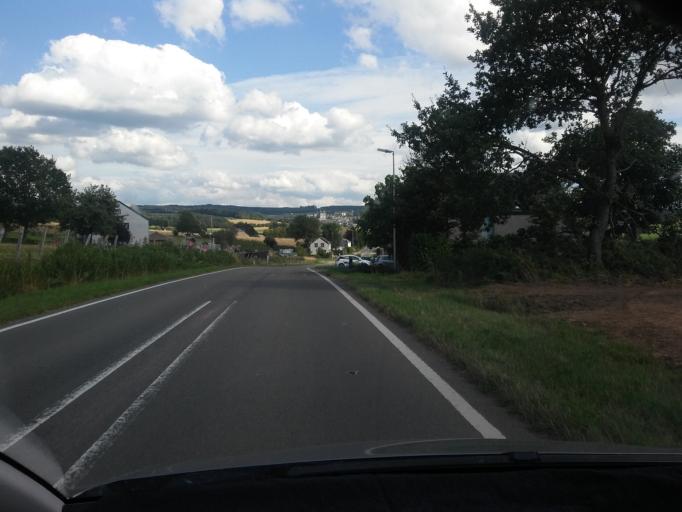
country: BE
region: Wallonia
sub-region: Province du Luxembourg
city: Saint-Hubert
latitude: 50.0300
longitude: 5.3373
